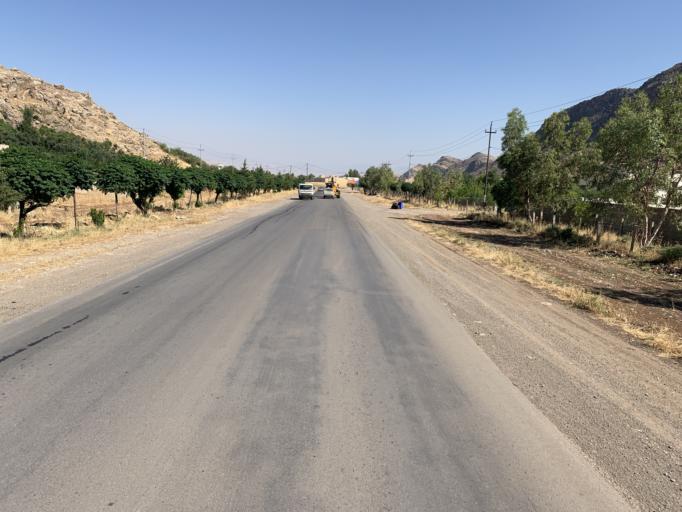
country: IQ
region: As Sulaymaniyah
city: Raniye
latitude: 36.2695
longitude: 44.8374
